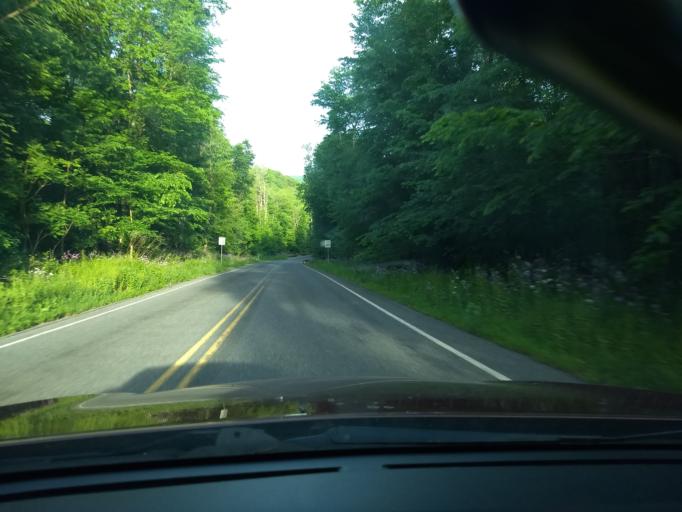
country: US
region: Pennsylvania
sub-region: Cambria County
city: Gallitzin
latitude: 40.5030
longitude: -78.5168
